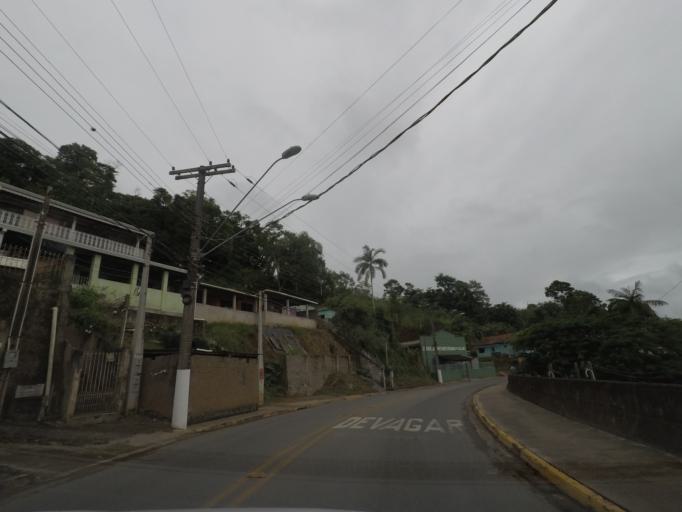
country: BR
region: Sao Paulo
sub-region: Cajati
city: Cajati
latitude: -24.7215
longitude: -48.1062
